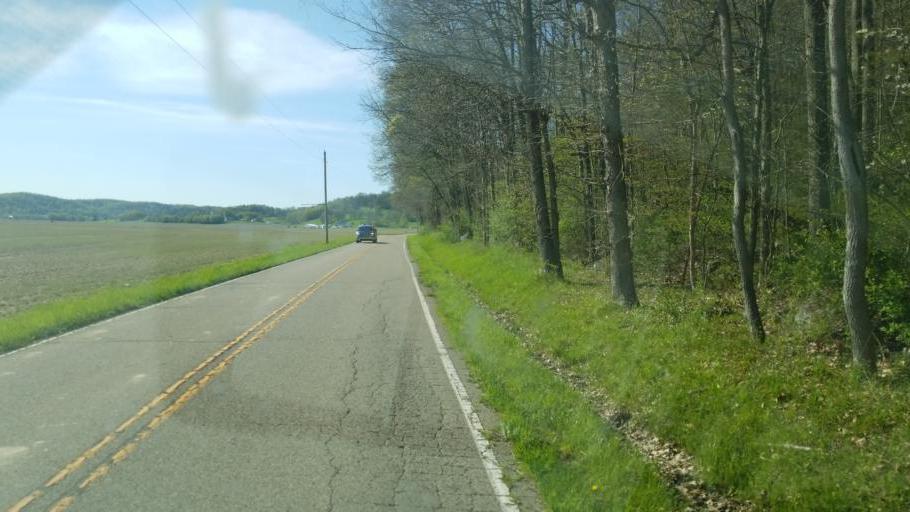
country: US
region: Ohio
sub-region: Coshocton County
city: Coshocton
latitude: 40.3588
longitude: -81.9570
